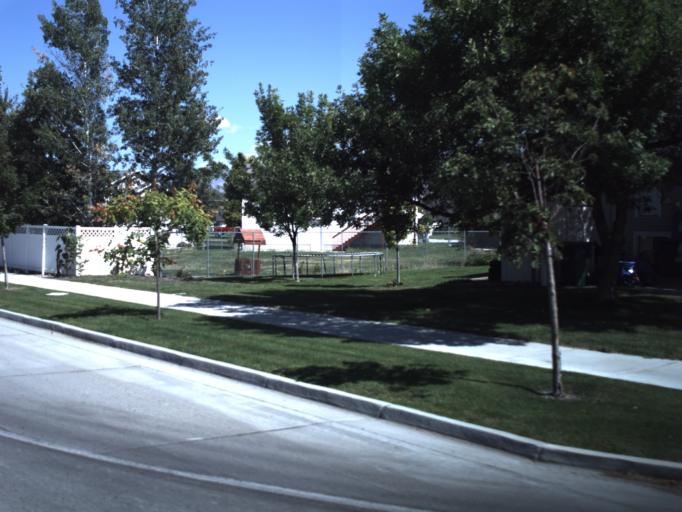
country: US
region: Utah
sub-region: Cache County
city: Logan
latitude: 41.7260
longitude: -111.8599
